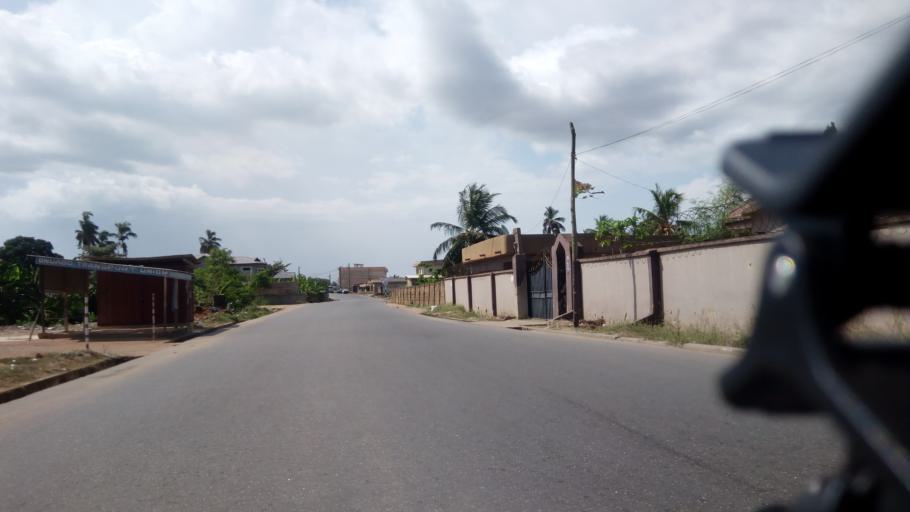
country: GH
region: Central
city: Cape Coast
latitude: 5.1316
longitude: -1.2773
